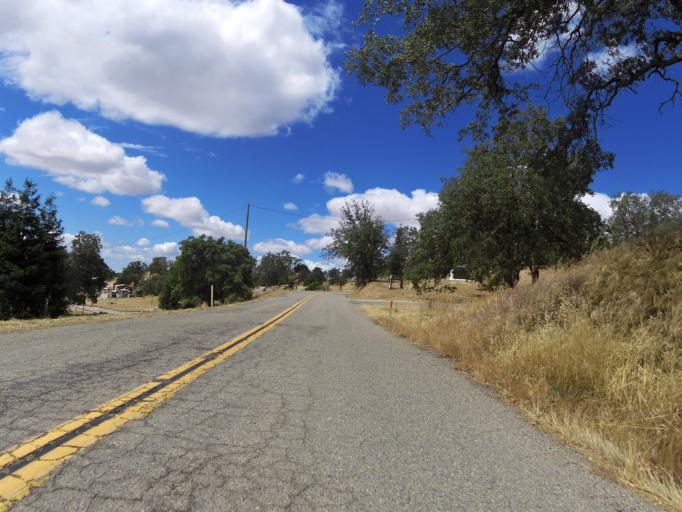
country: US
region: California
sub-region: Madera County
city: Yosemite Lakes
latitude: 37.2051
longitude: -119.8918
